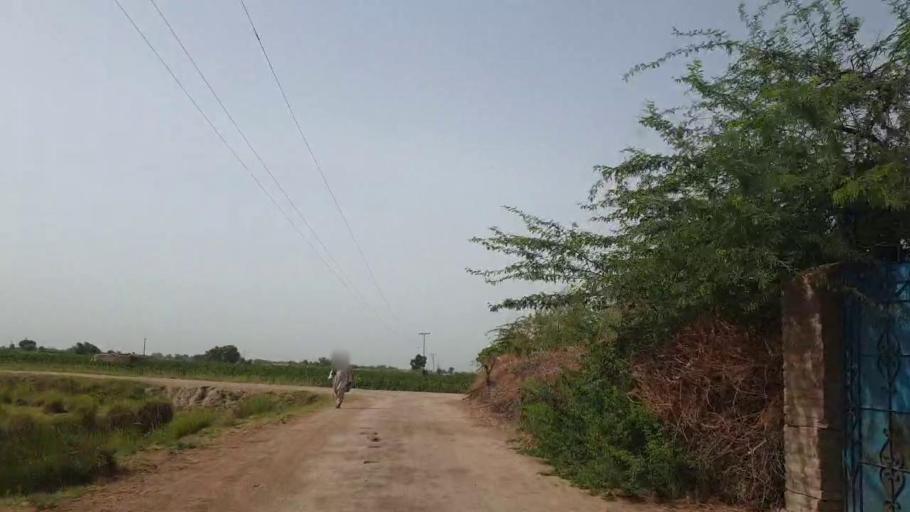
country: PK
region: Sindh
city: Nawabshah
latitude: 26.1097
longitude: 68.4438
